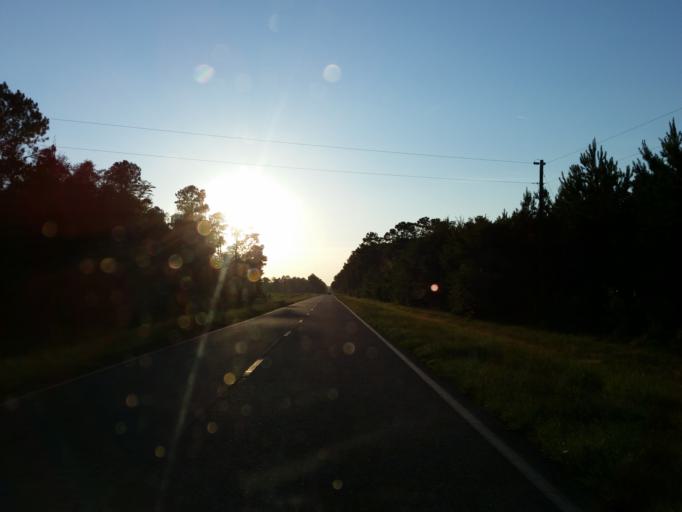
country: US
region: Georgia
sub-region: Lanier County
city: Lakeland
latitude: 31.1697
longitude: -83.1045
